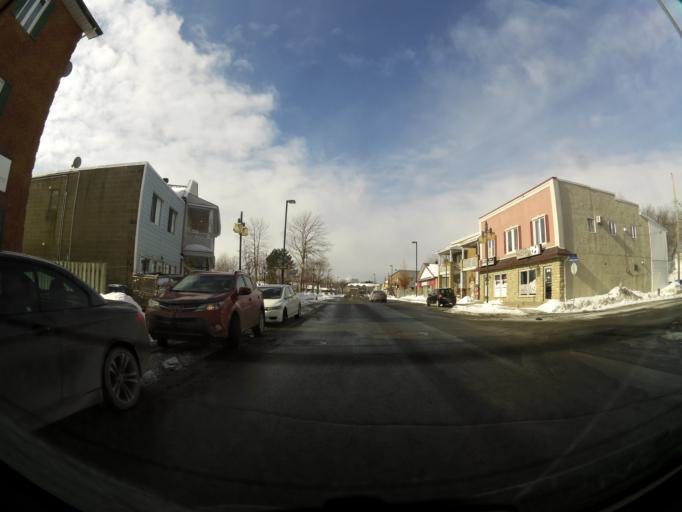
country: CA
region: Quebec
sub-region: Outaouais
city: Gatineau
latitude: 45.4815
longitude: -75.6411
